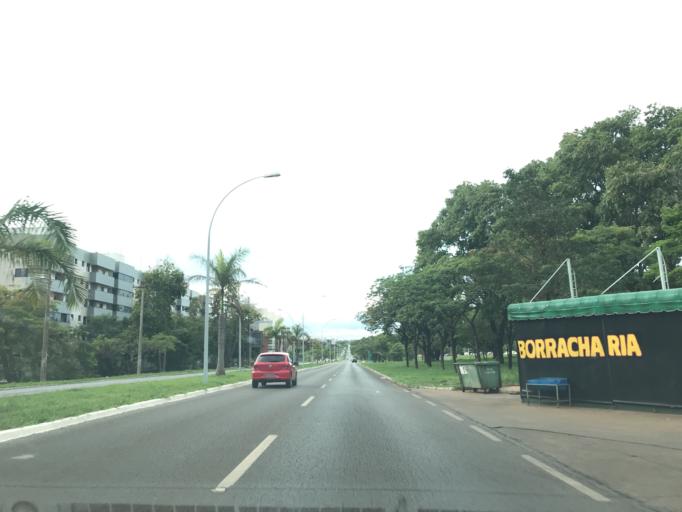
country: BR
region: Federal District
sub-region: Brasilia
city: Brasilia
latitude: -15.7436
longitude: -47.8894
